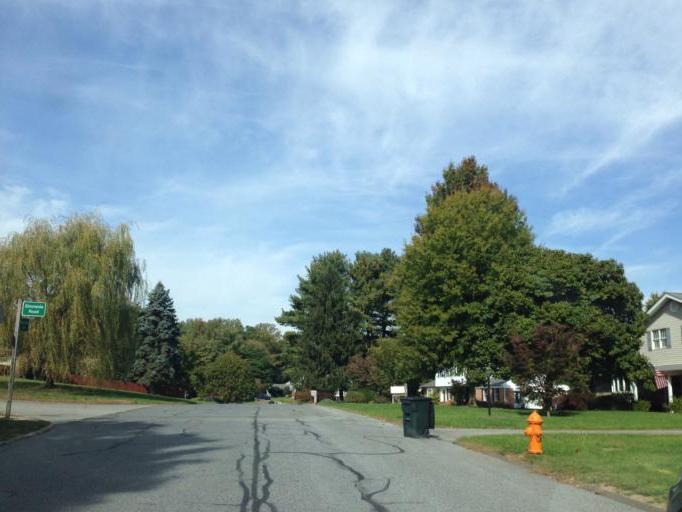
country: US
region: Maryland
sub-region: Howard County
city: Columbia
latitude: 39.2850
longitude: -76.8502
